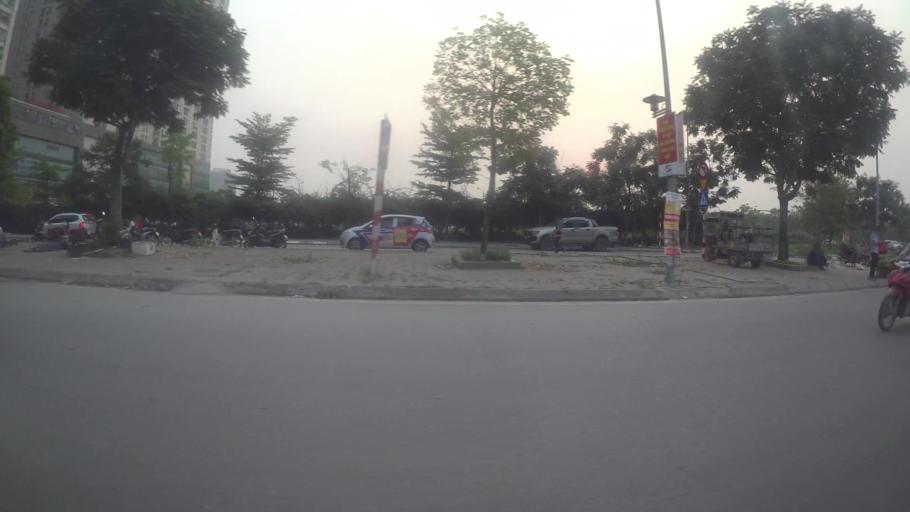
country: VN
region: Ha Noi
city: Cau Dien
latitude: 21.0095
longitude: 105.7308
